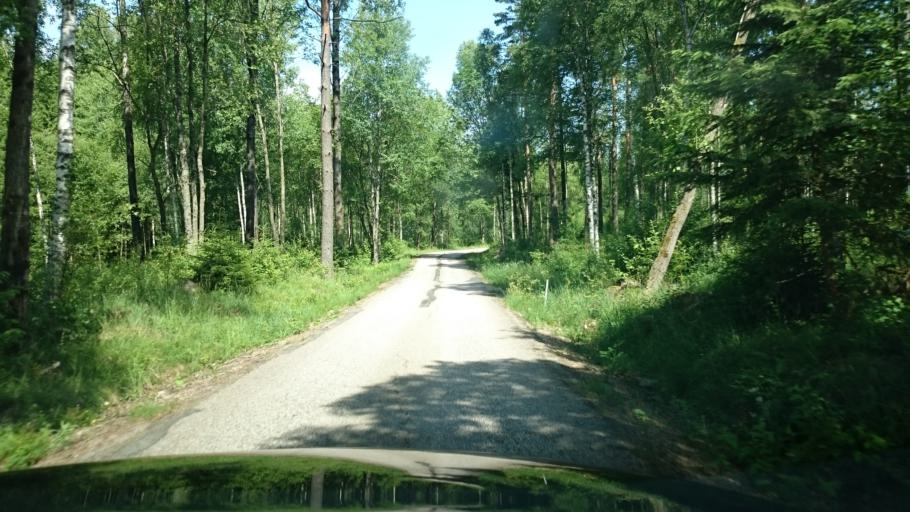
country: SE
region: Halland
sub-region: Hylte Kommun
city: Hyltebruk
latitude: 56.9778
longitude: 13.2070
